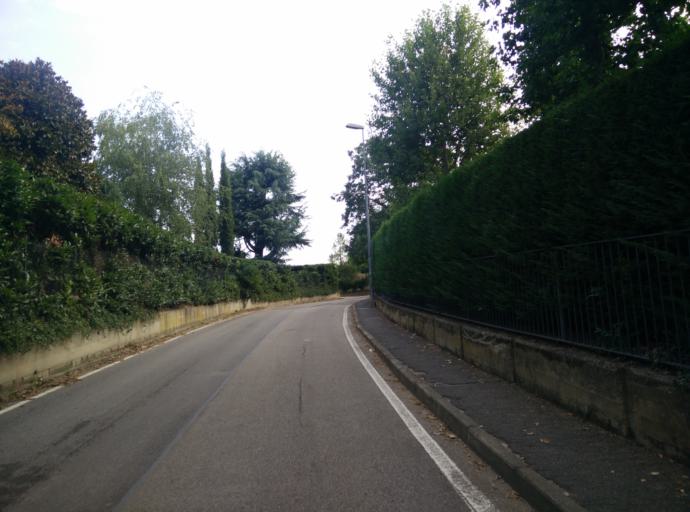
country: IT
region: Piedmont
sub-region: Provincia di Torino
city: Revigliasco
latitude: 44.9956
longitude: 7.7229
